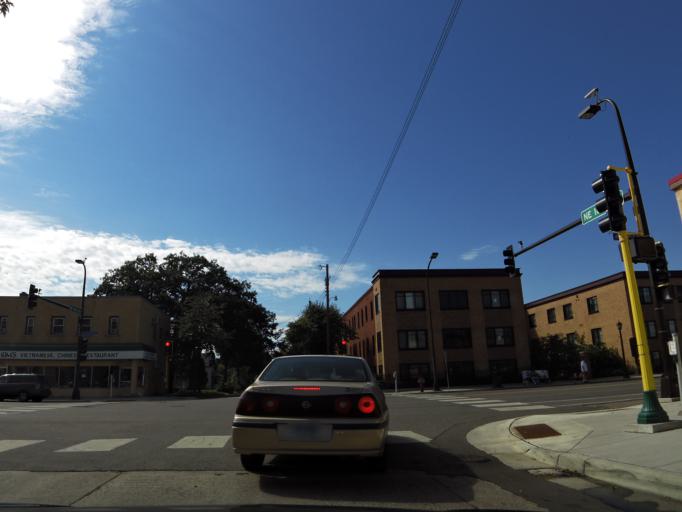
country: US
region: Minnesota
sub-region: Hennepin County
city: Minneapolis
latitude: 45.0069
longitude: -93.2471
